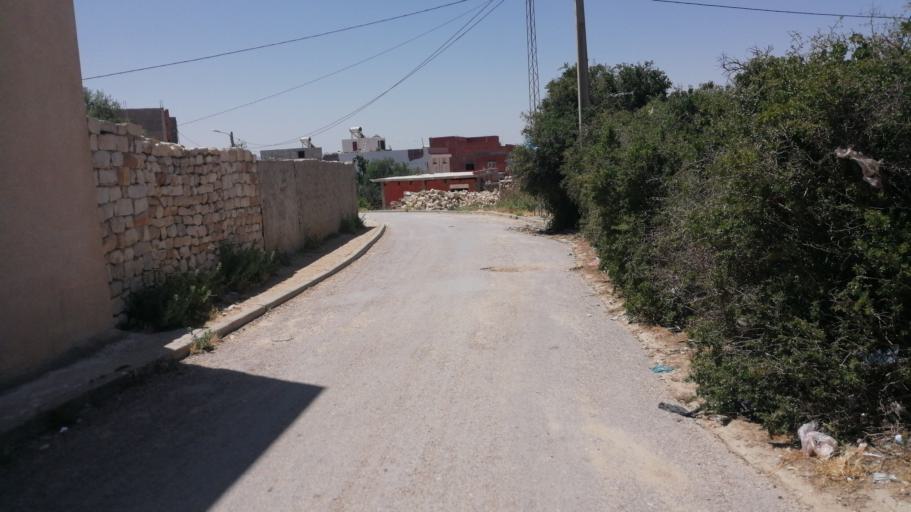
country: TN
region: Silyanah
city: Maktar
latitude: 35.8508
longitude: 9.2039
